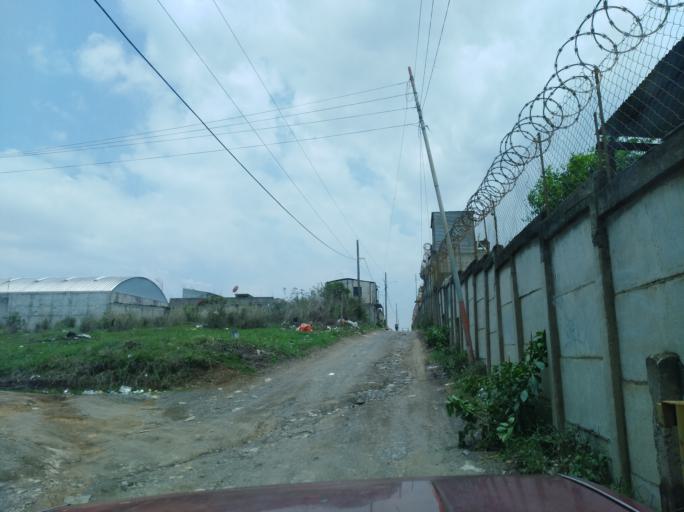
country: GT
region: Guatemala
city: Villa Nueva
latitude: 14.5283
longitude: -90.6244
